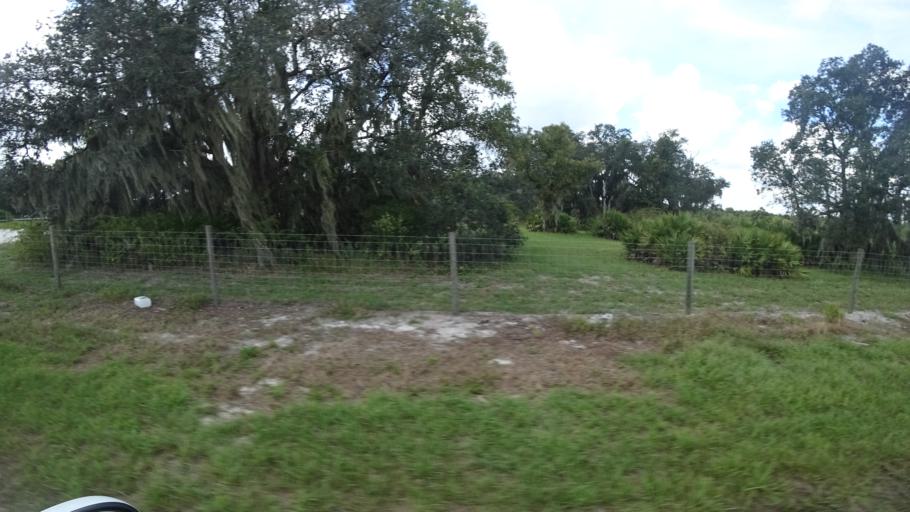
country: US
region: Florida
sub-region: Hillsborough County
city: Wimauma
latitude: 27.6288
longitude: -82.2310
